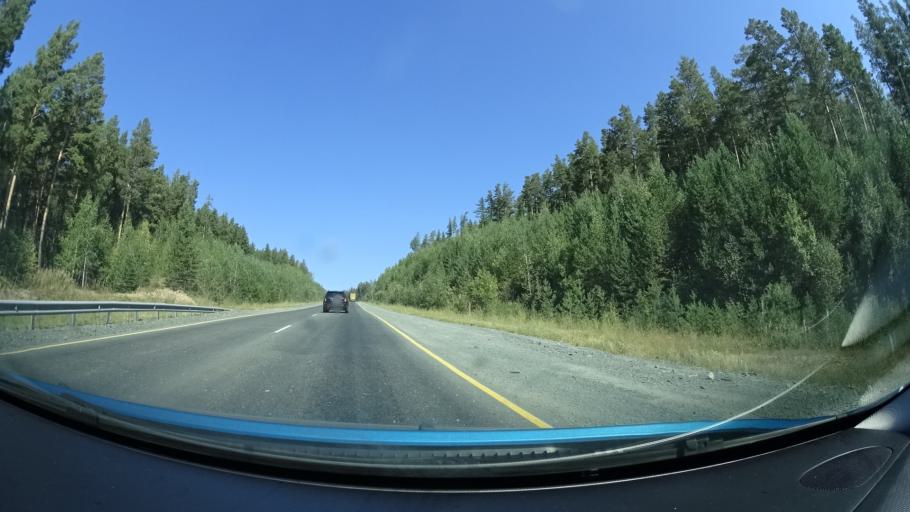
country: RU
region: Bashkortostan
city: Abzakovo
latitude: 53.8829
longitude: 58.5298
